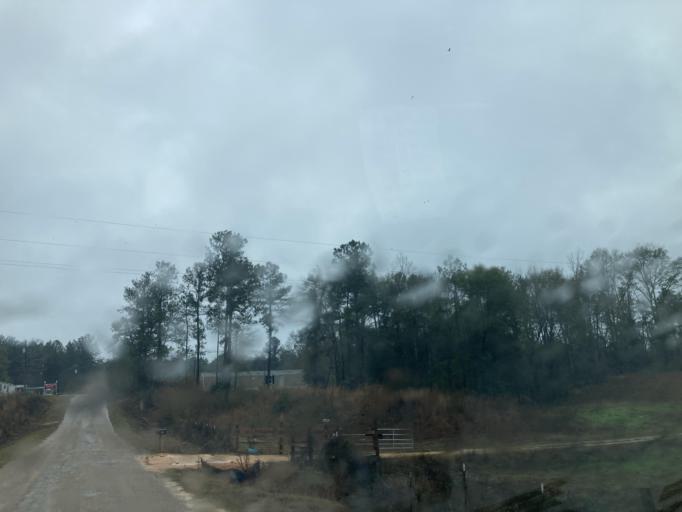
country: US
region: Mississippi
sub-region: Forrest County
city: Rawls Springs
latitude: 31.4381
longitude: -89.3483
